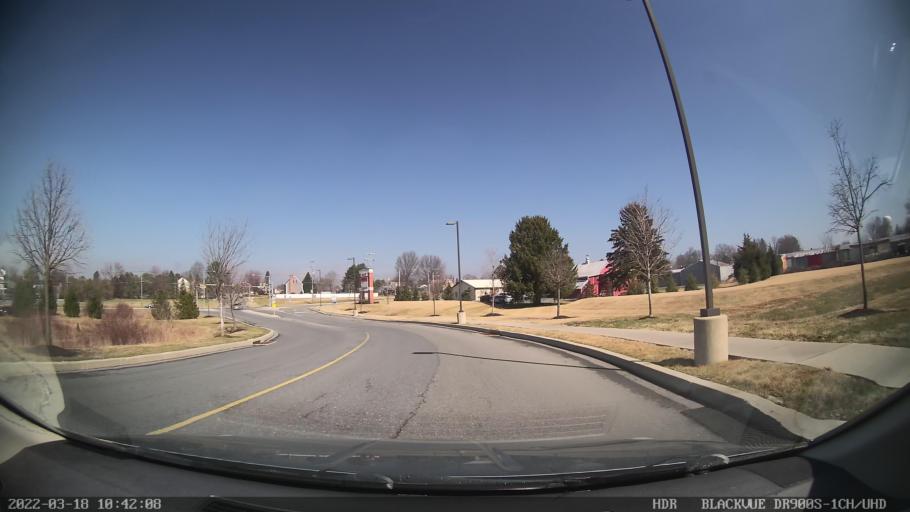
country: US
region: Pennsylvania
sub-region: Berks County
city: Kutztown
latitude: 40.5049
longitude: -75.7892
